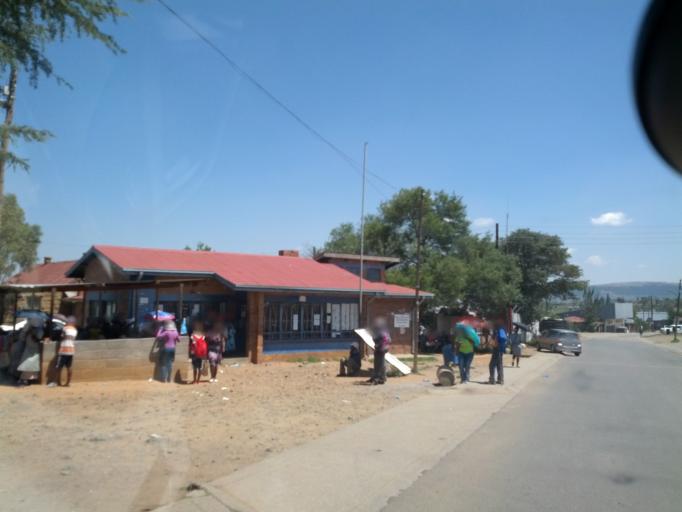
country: LS
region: Butha-Buthe
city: Butha-Buthe
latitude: -28.7631
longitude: 28.2484
